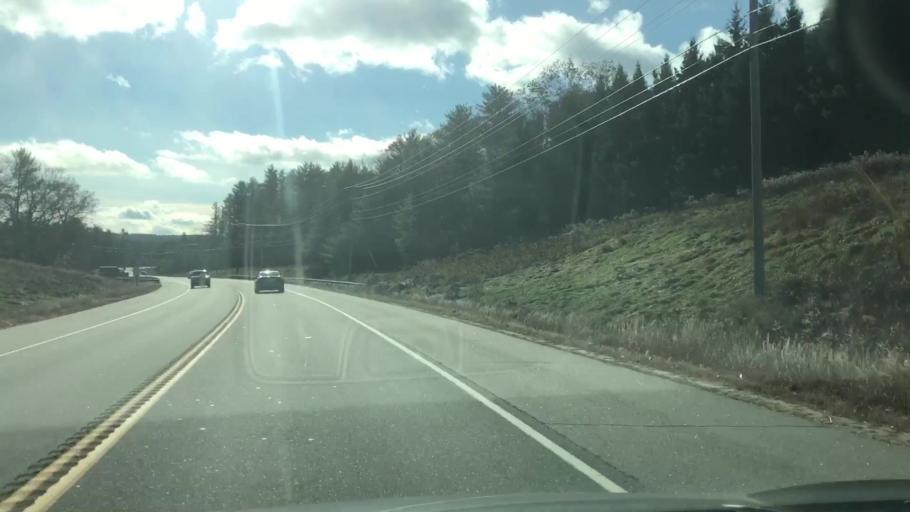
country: US
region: New Hampshire
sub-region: Belknap County
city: Barnstead
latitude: 43.3251
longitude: -71.3050
